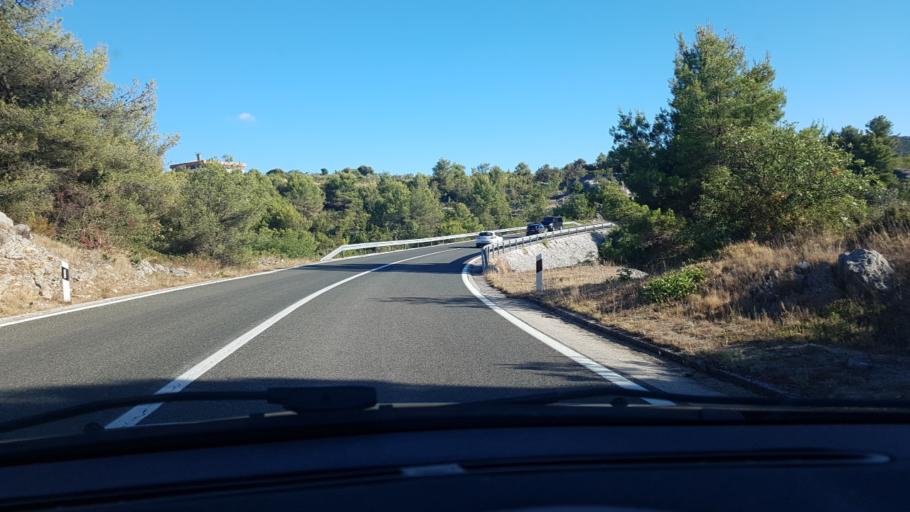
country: HR
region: Sibensko-Kniniska
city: Primosten
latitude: 43.5862
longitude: 15.9359
